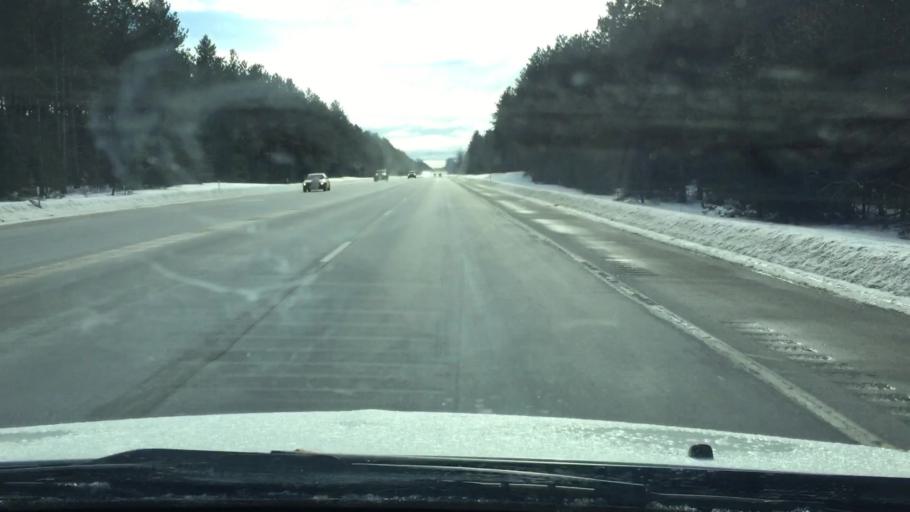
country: US
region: Michigan
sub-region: Kalkaska County
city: Kalkaska
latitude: 44.8110
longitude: -85.1420
